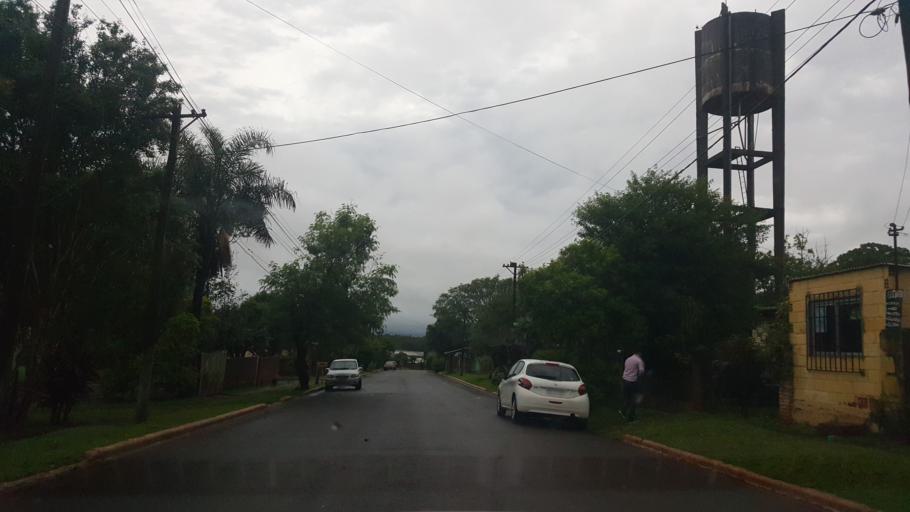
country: AR
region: Misiones
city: Santo Pipo
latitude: -27.1422
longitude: -55.4099
